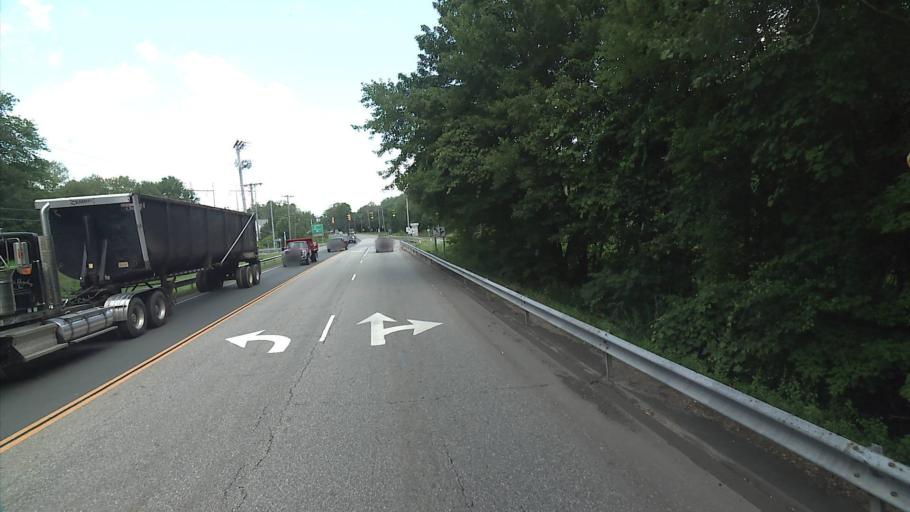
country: US
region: Connecticut
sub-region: Middlesex County
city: Deep River Center
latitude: 41.3637
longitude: -72.4242
